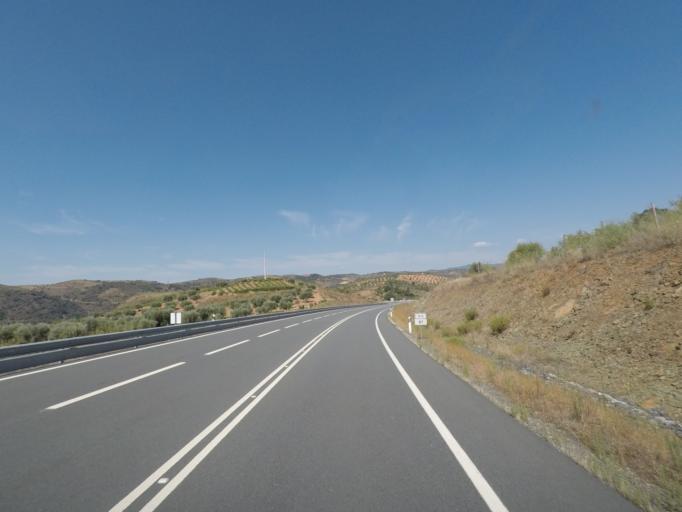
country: PT
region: Braganca
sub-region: Alfandega da Fe
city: Alfandega da Fe
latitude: 41.3050
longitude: -6.9050
